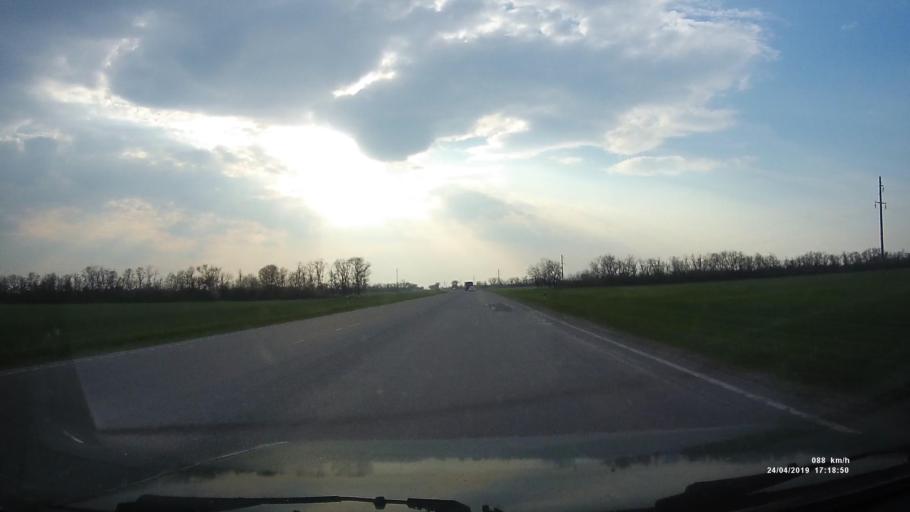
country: RU
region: Rostov
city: Gigant
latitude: 46.5139
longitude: 41.3798
